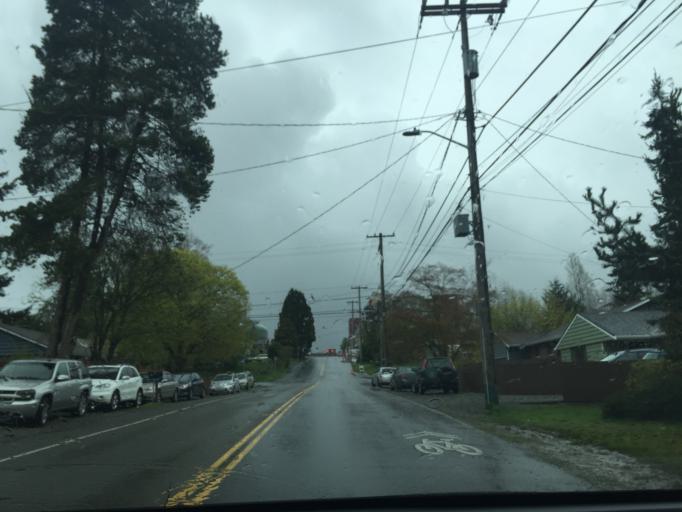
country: US
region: Washington
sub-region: King County
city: Shoreline
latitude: 47.7594
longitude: -122.3174
